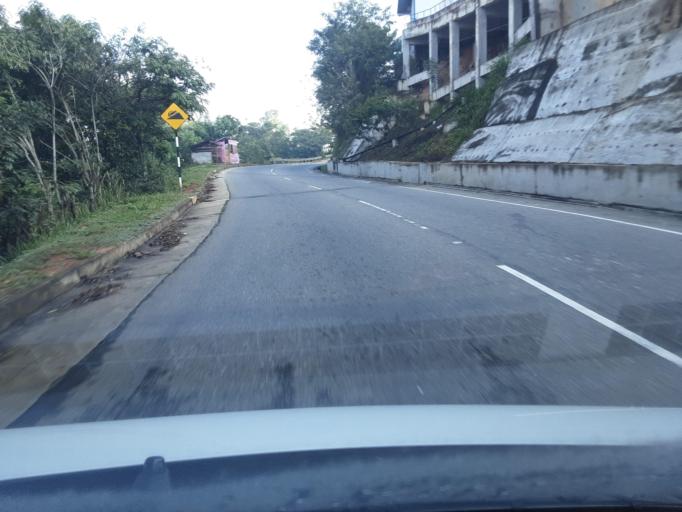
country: LK
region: Uva
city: Badulla
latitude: 6.9186
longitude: 80.9576
